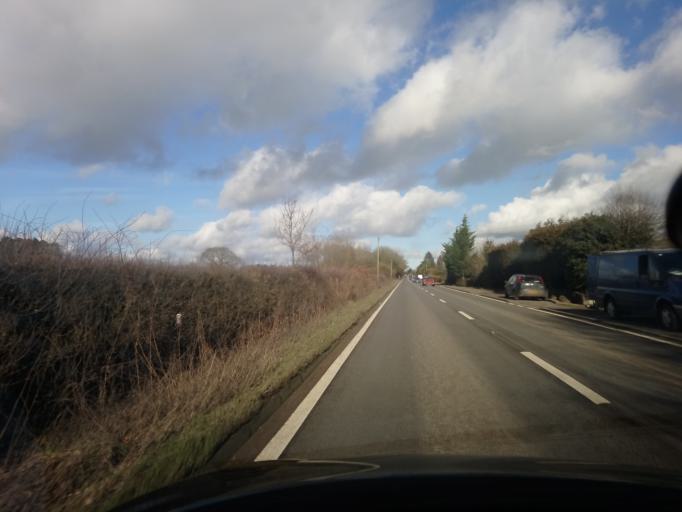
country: GB
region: England
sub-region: Shropshire
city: Astley
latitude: 52.7542
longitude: -2.7165
